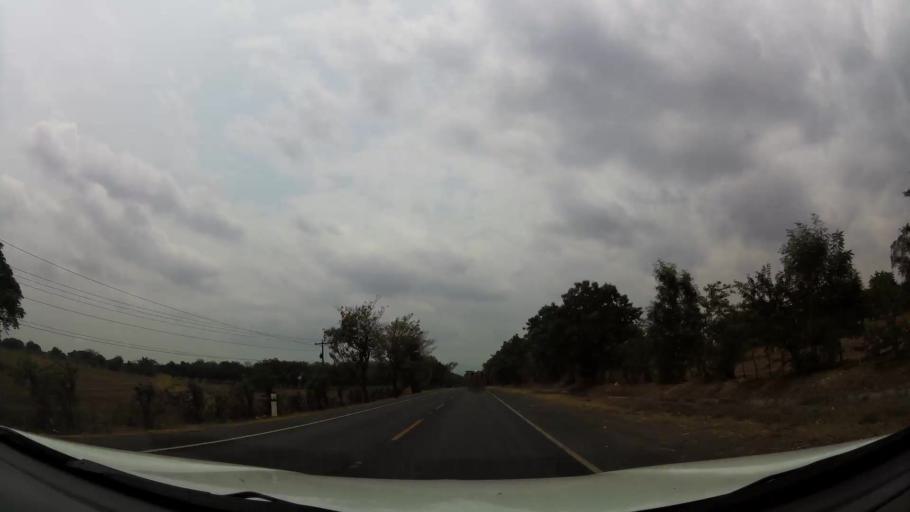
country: NI
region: Leon
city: Telica
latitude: 12.5005
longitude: -86.8600
